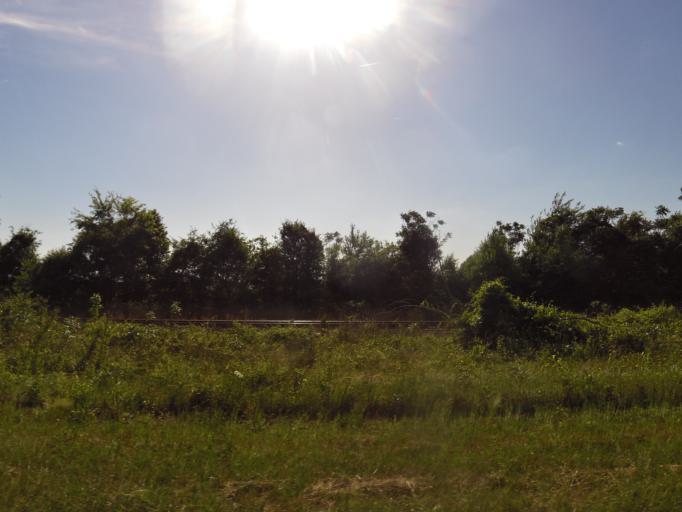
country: US
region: South Carolina
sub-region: Allendale County
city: Fairfax
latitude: 32.9317
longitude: -81.2372
